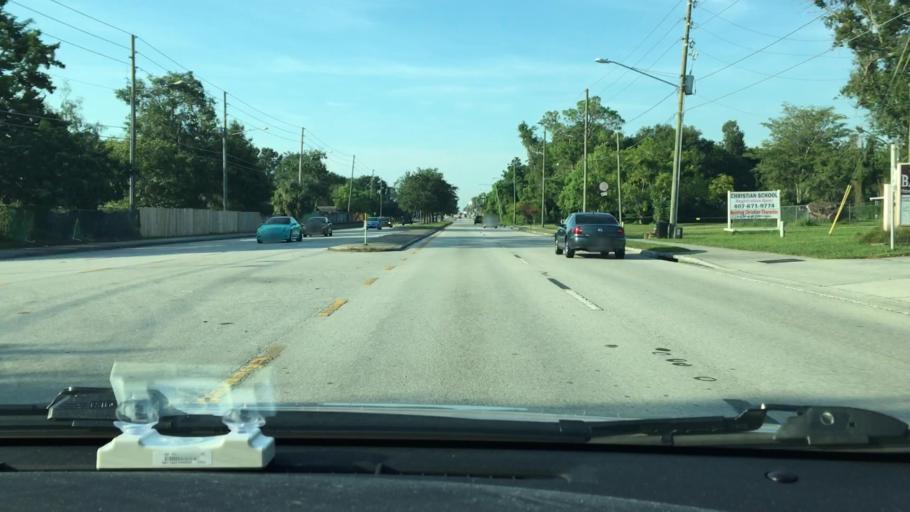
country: US
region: Florida
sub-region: Orange County
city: Union Park
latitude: 28.5788
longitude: -81.2862
